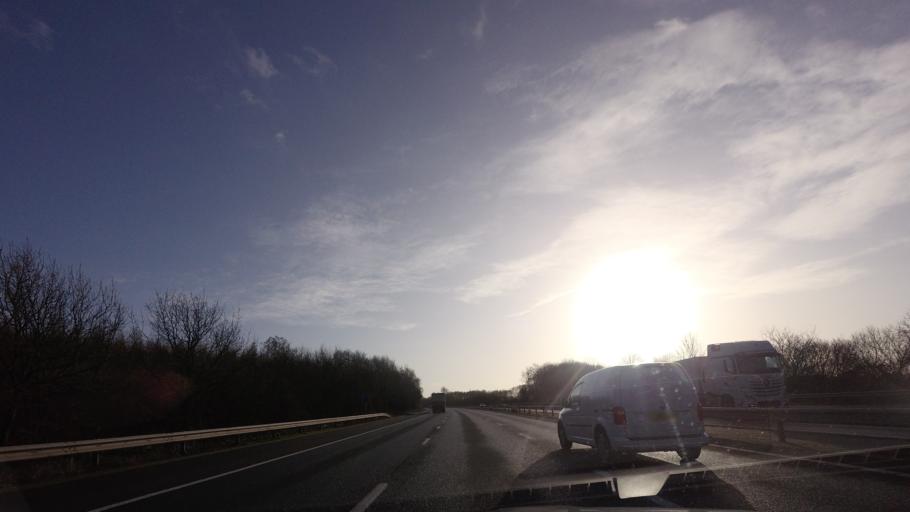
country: GB
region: England
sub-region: Kent
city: Borough Green
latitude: 51.3288
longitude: 0.2737
